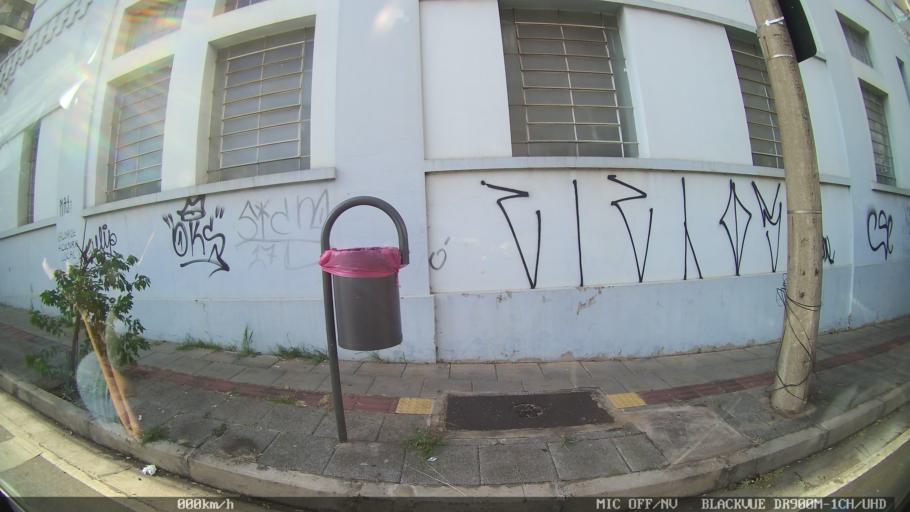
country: BR
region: Sao Paulo
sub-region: Sao Jose Do Rio Preto
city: Sao Jose do Rio Preto
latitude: -20.8153
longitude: -49.3835
